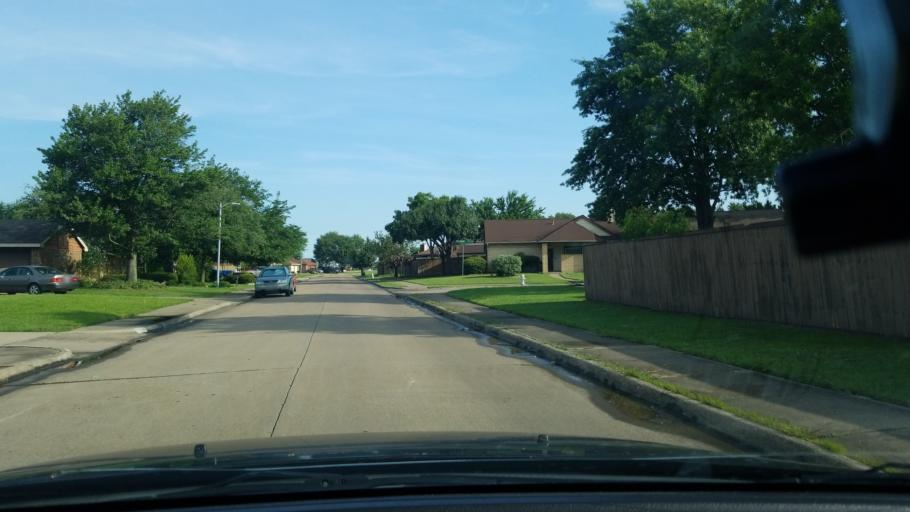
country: US
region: Texas
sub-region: Dallas County
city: Mesquite
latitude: 32.8032
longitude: -96.6087
